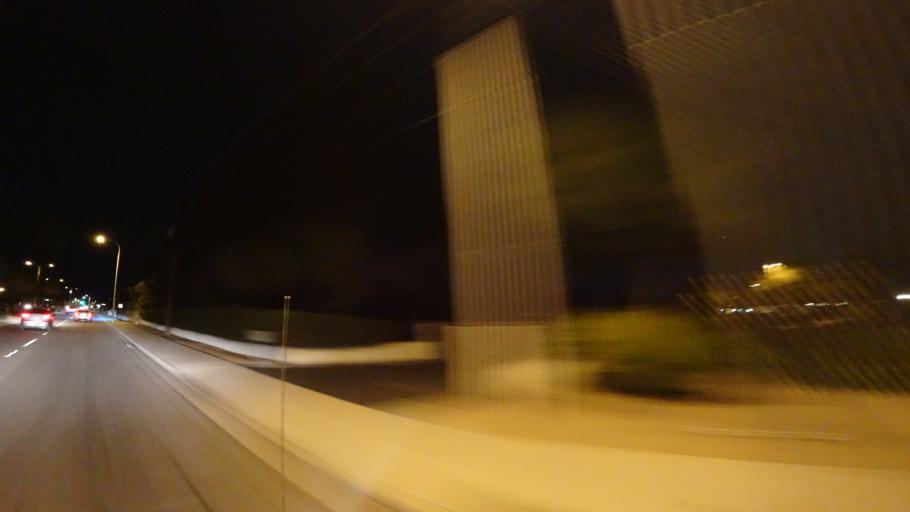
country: US
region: Arizona
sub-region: Maricopa County
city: Chandler
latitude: 33.3173
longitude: -111.8243
